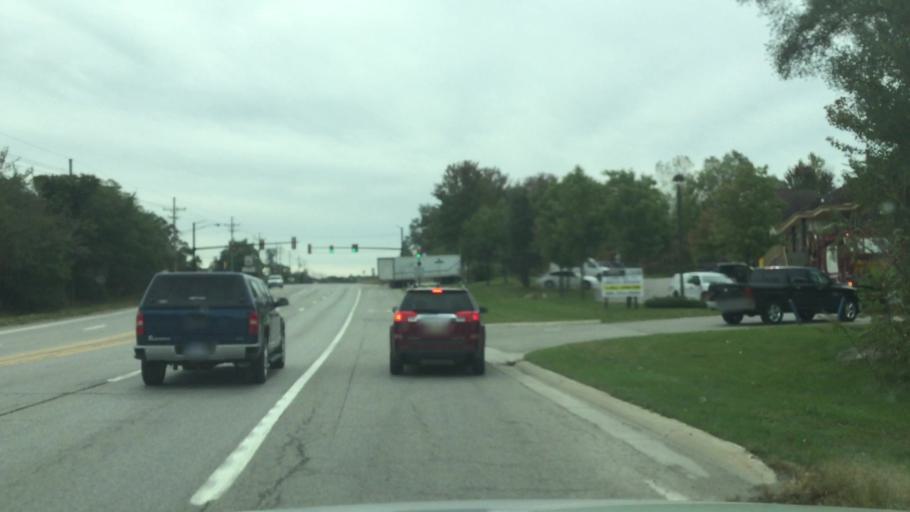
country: US
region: Michigan
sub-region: Oakland County
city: Clarkston
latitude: 42.7604
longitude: -83.4829
